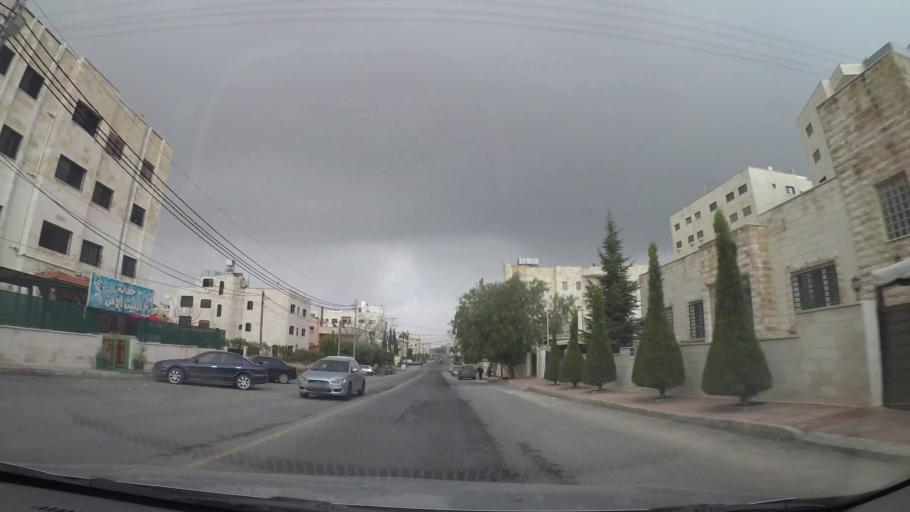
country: JO
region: Amman
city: Umm as Summaq
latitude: 31.8858
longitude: 35.8519
